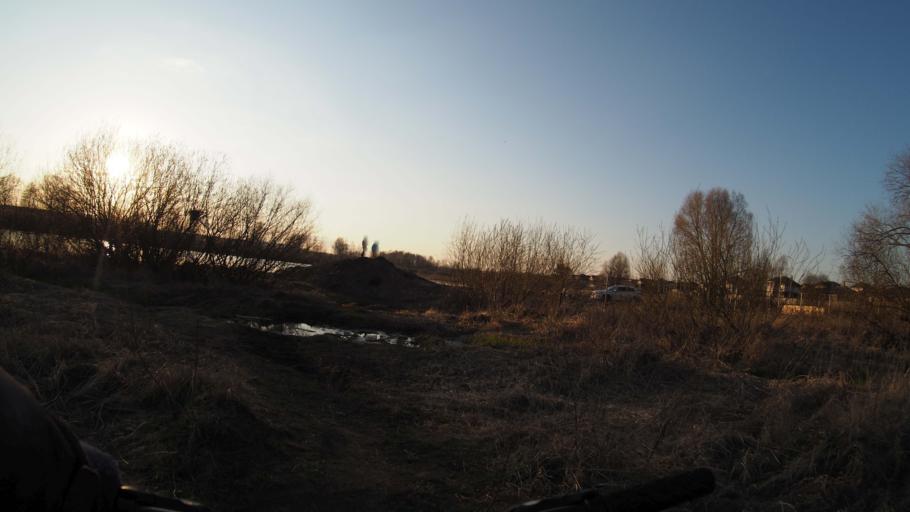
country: RU
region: Moskovskaya
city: Ramenskoye
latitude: 55.5582
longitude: 38.2963
